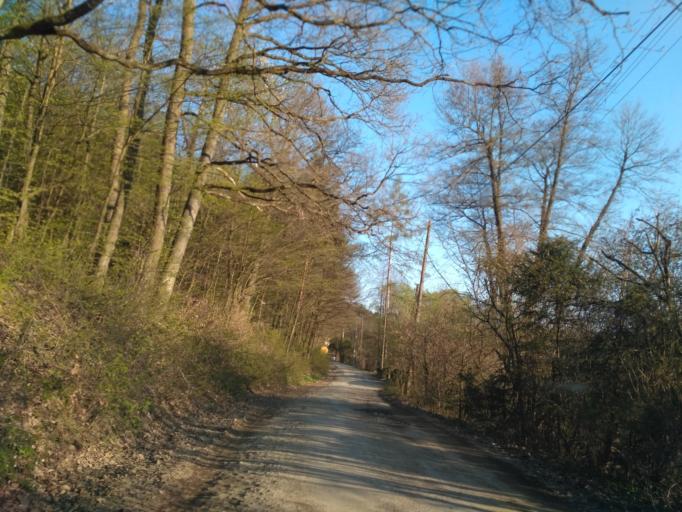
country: SK
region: Kosicky
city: Kosice
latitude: 48.7339
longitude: 21.1595
